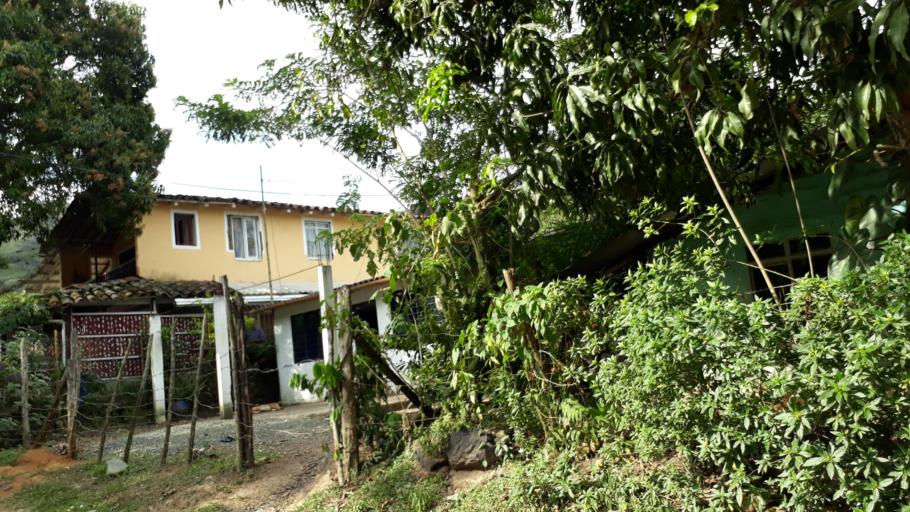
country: CO
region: Valle del Cauca
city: Jamundi
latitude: 3.2197
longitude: -76.6256
